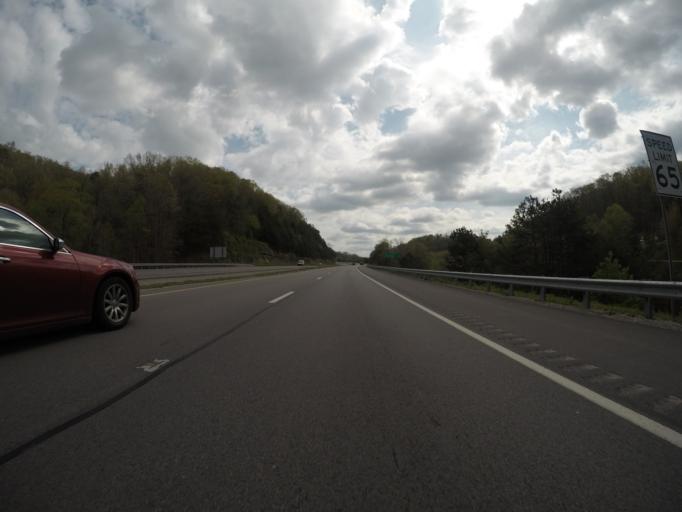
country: US
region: West Virginia
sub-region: Kanawha County
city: Alum Creek
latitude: 38.2784
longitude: -81.7733
